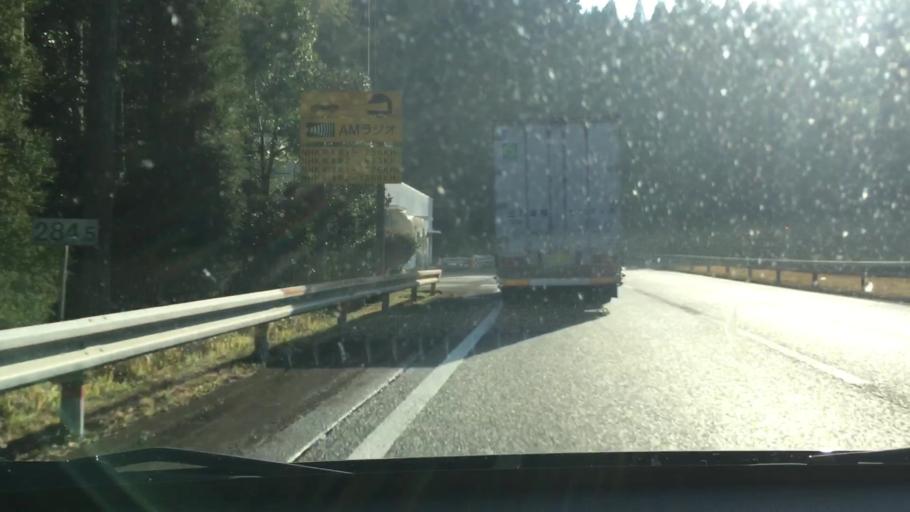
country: JP
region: Kagoshima
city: Okuchi-shinohara
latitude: 31.9833
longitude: 130.7516
